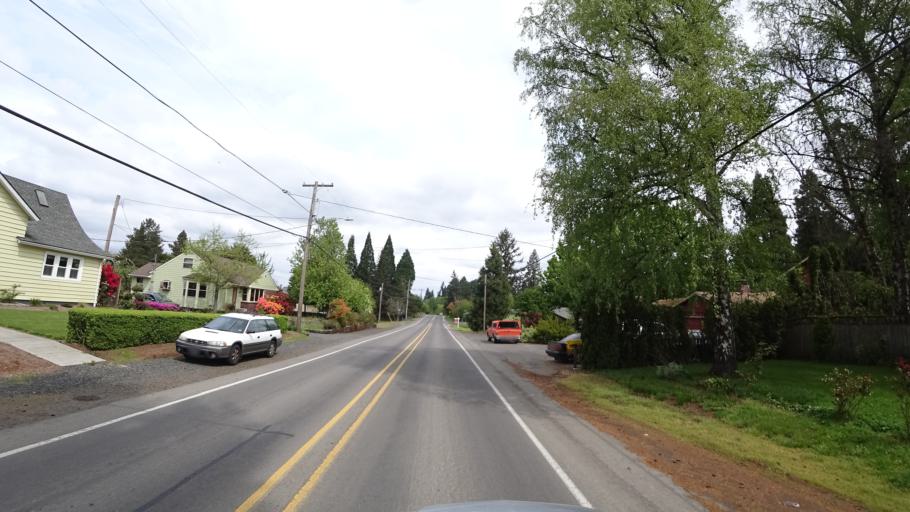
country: US
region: Oregon
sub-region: Washington County
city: Hillsboro
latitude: 45.5321
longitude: -122.9933
